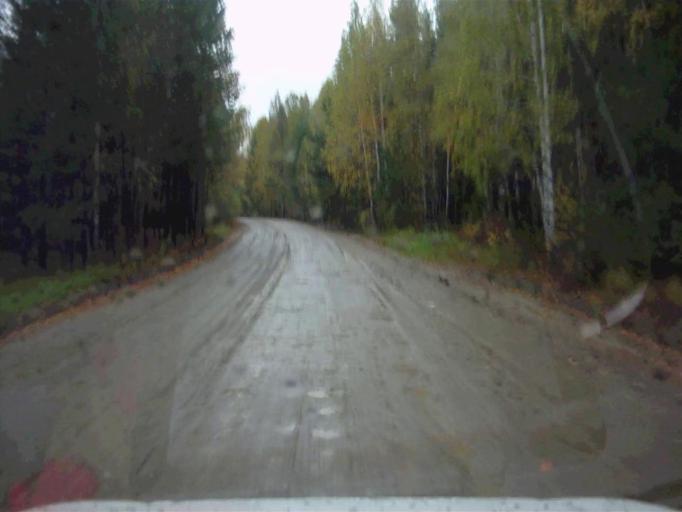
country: RU
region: Chelyabinsk
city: Kyshtym
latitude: 55.7483
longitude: 60.4892
